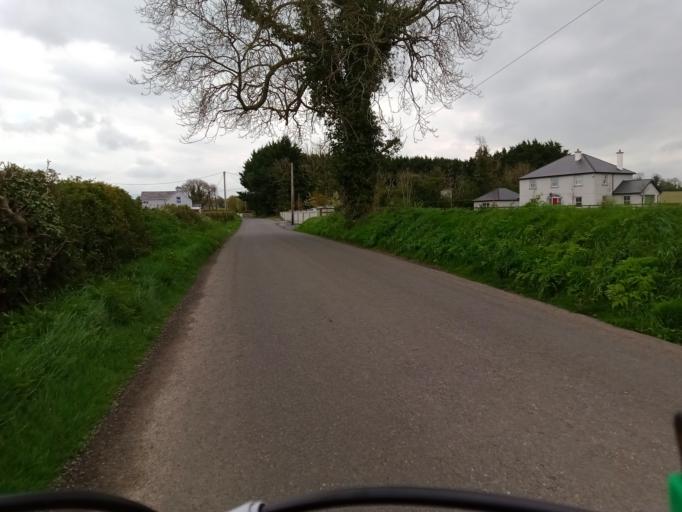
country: IE
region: Leinster
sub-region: Kilkenny
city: Kilkenny
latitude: 52.6183
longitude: -7.2555
